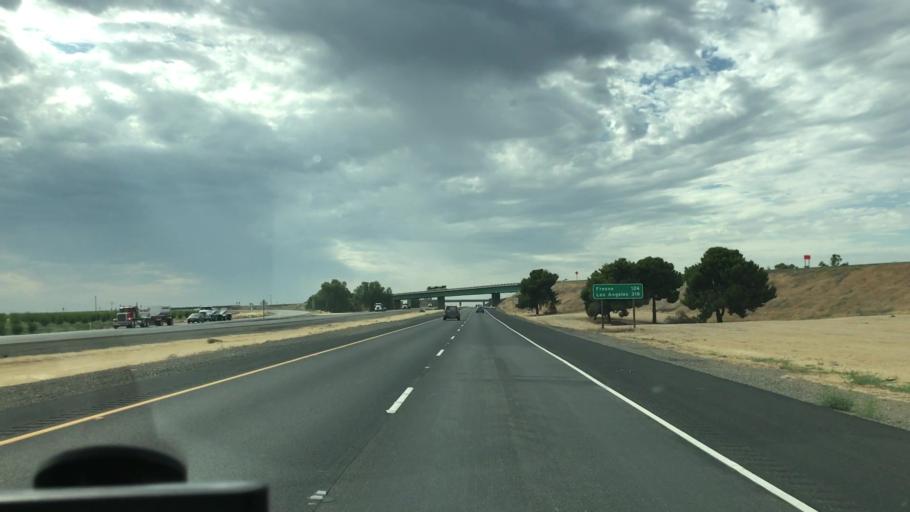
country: US
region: California
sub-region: San Joaquin County
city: Tracy
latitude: 37.6409
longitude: -121.4059
